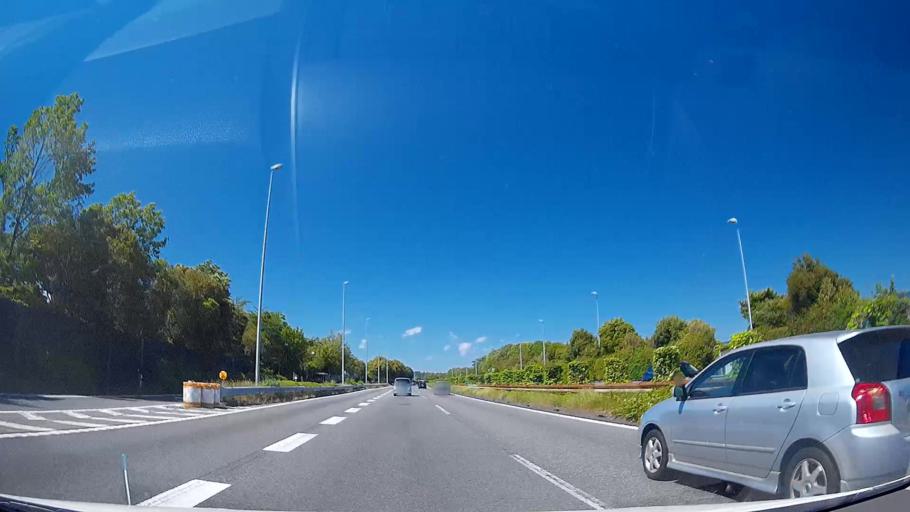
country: JP
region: Shizuoka
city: Mishima
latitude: 35.2034
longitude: 138.9022
